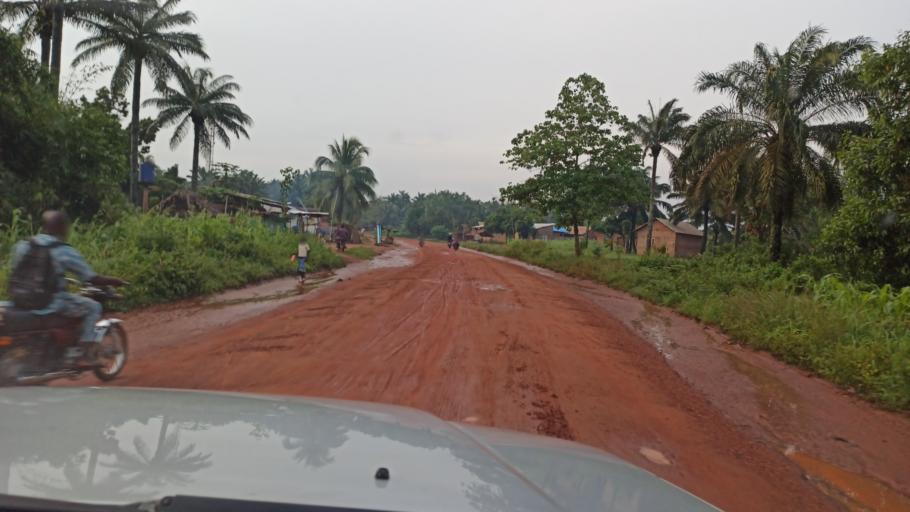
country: BJ
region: Queme
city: Porto-Novo
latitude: 6.5481
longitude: 2.6124
